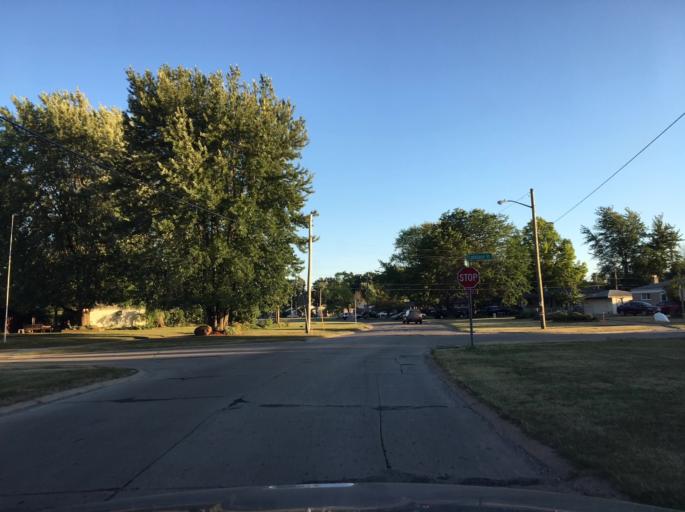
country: US
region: Michigan
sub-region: Macomb County
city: Clinton
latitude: 42.5510
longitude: -82.9102
